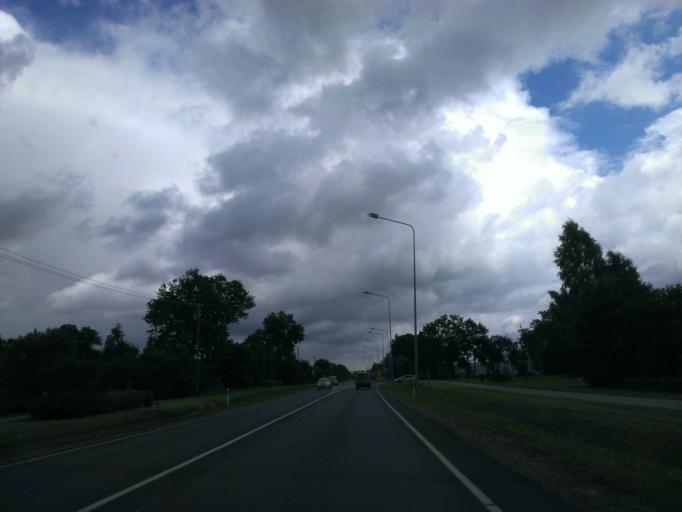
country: LV
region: Sigulda
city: Sigulda
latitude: 57.1439
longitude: 24.8506
